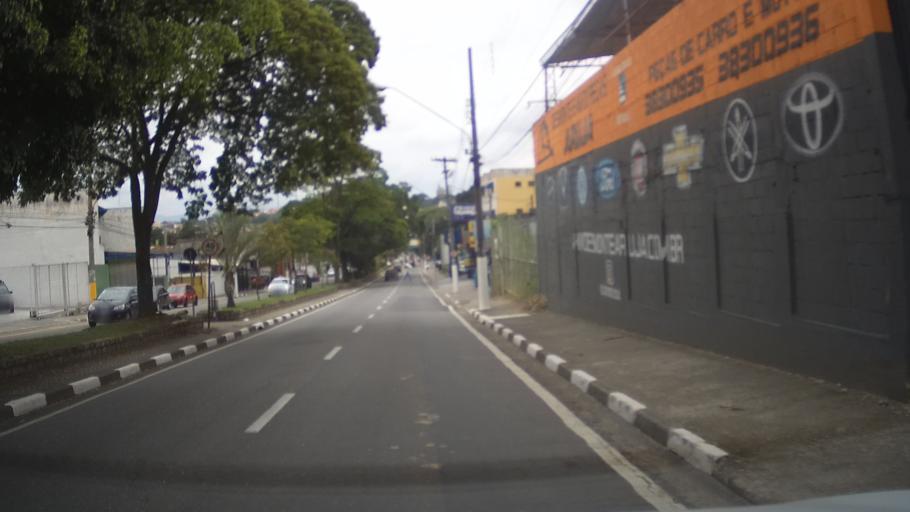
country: BR
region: Sao Paulo
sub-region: Aruja
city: Aruja
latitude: -23.4000
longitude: -46.3186
